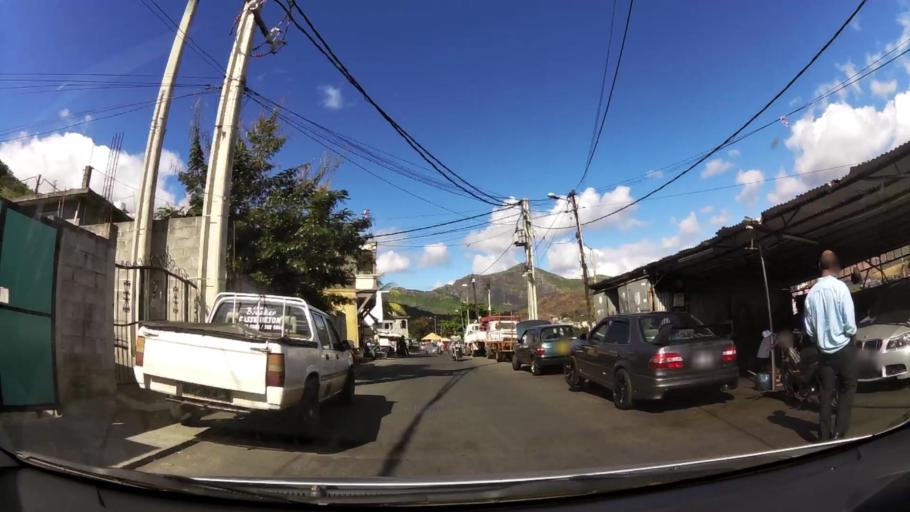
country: MU
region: Port Louis
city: Port Louis
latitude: -20.1625
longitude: 57.5194
